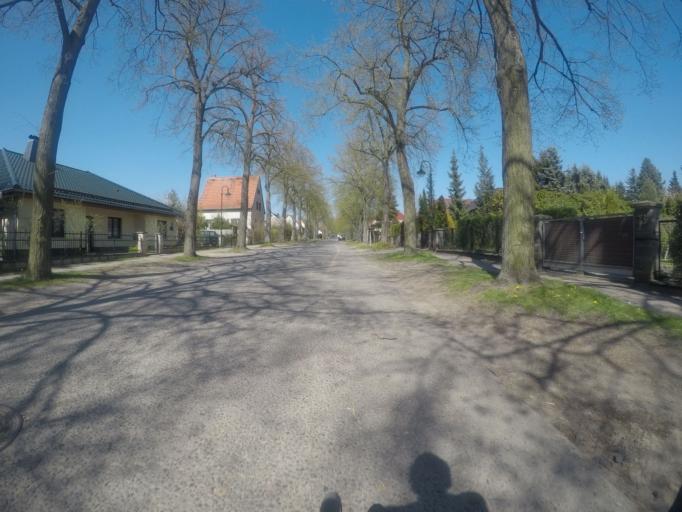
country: DE
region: Brandenburg
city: Bernau bei Berlin
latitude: 52.6825
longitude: 13.5902
